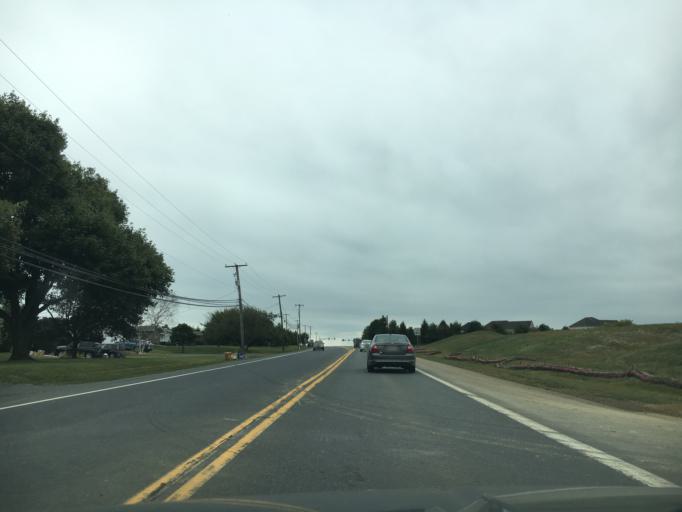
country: US
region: Pennsylvania
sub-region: Northampton County
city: Bath
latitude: 40.6893
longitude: -75.3915
